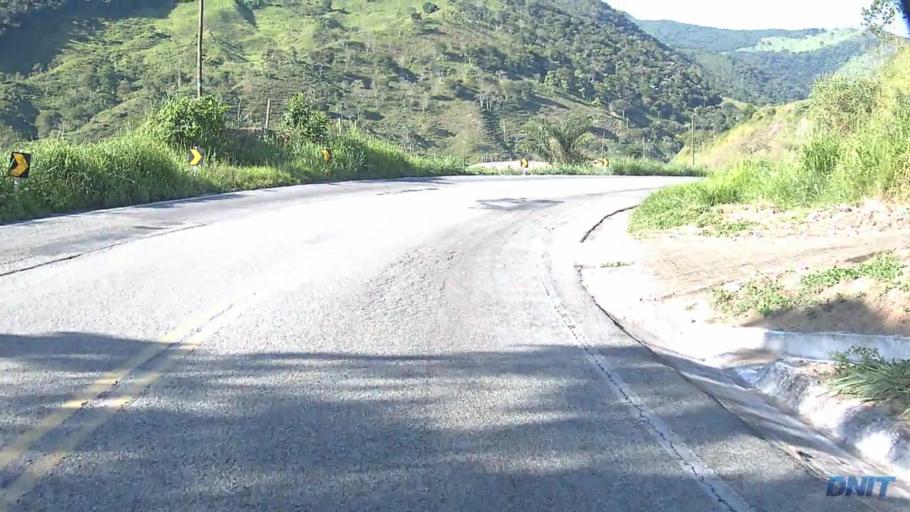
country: BR
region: Minas Gerais
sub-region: Nova Era
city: Nova Era
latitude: -19.6489
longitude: -42.9325
